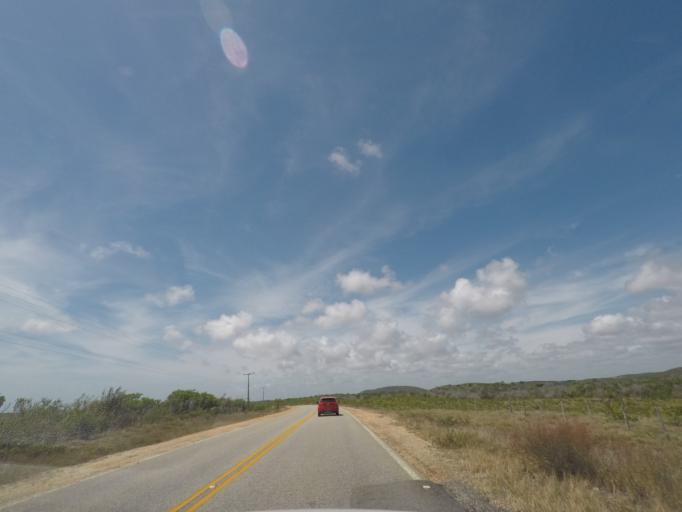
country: BR
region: Sergipe
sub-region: Sao Cristovao
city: Sao Cristovao
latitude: -11.1557
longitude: -37.2023
